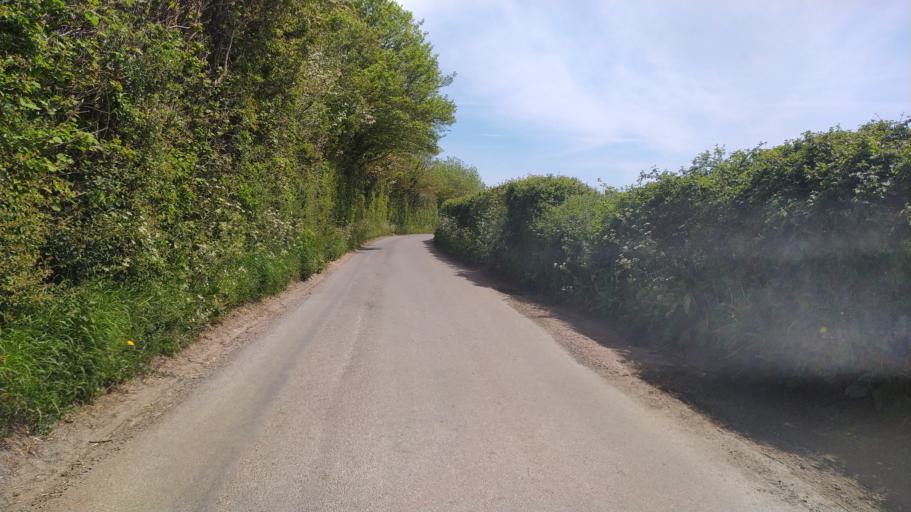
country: GB
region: England
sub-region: Dorset
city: Manston
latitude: 50.9446
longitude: -2.2294
